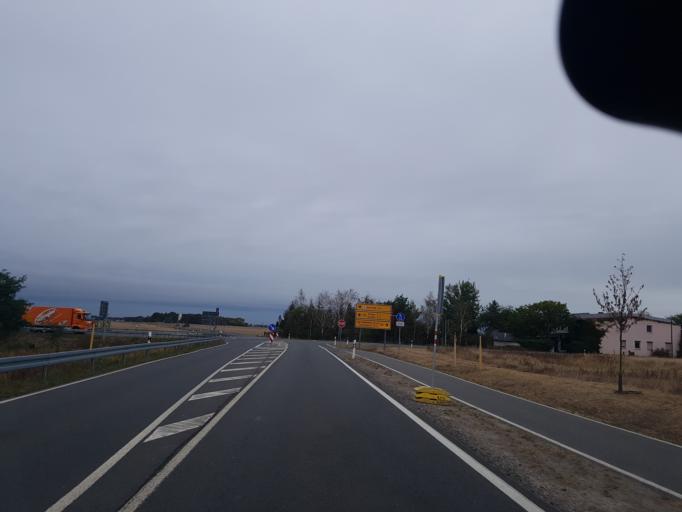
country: DE
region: Saxony
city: Beilrode
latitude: 51.5490
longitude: 13.0863
